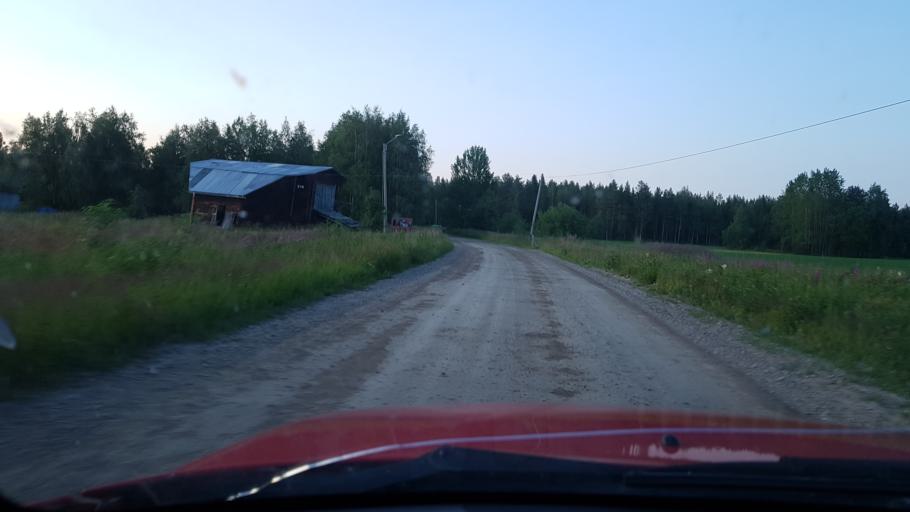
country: SE
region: Norrbotten
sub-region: Alvsbyns Kommun
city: AElvsbyn
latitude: 65.6995
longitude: 20.6769
